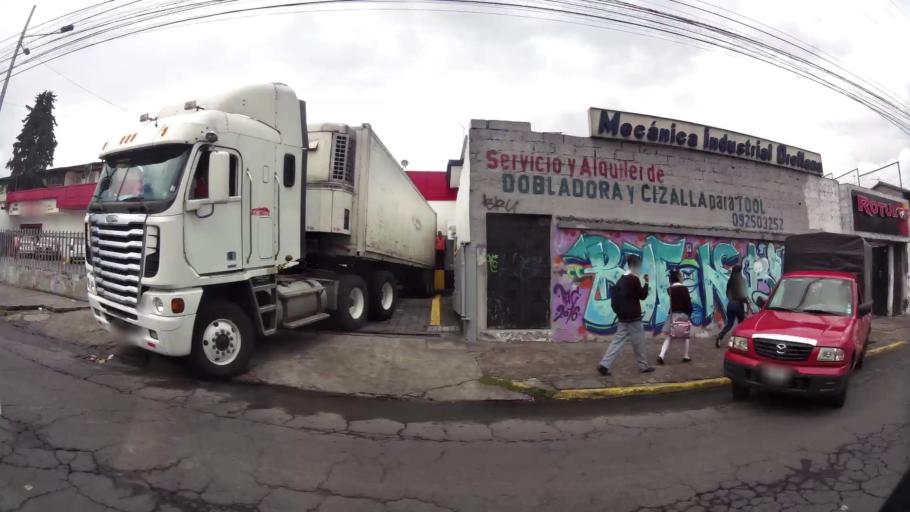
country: EC
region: Pichincha
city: Quito
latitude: -0.2720
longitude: -78.5522
